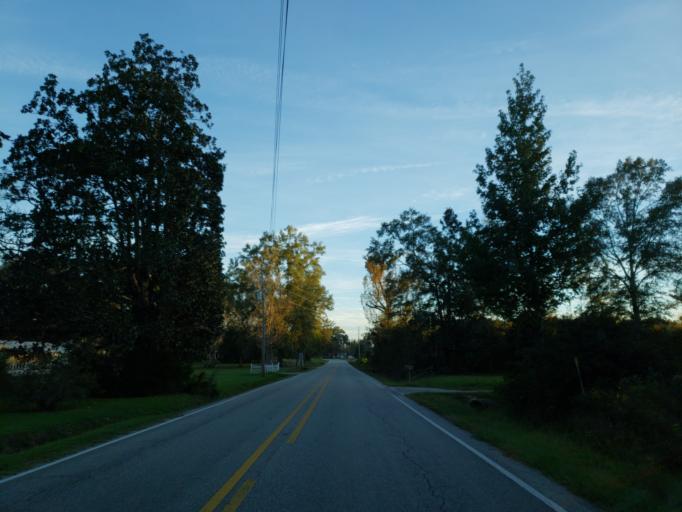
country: US
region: Mississippi
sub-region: Wayne County
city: Belmont
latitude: 31.4309
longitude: -88.4726
